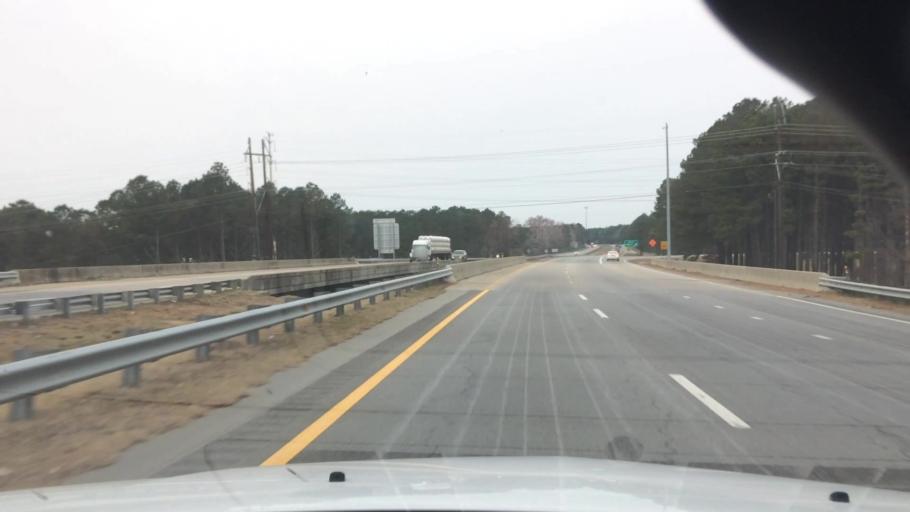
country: US
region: North Carolina
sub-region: Nash County
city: Rocky Mount
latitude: 35.9655
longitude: -77.8169
